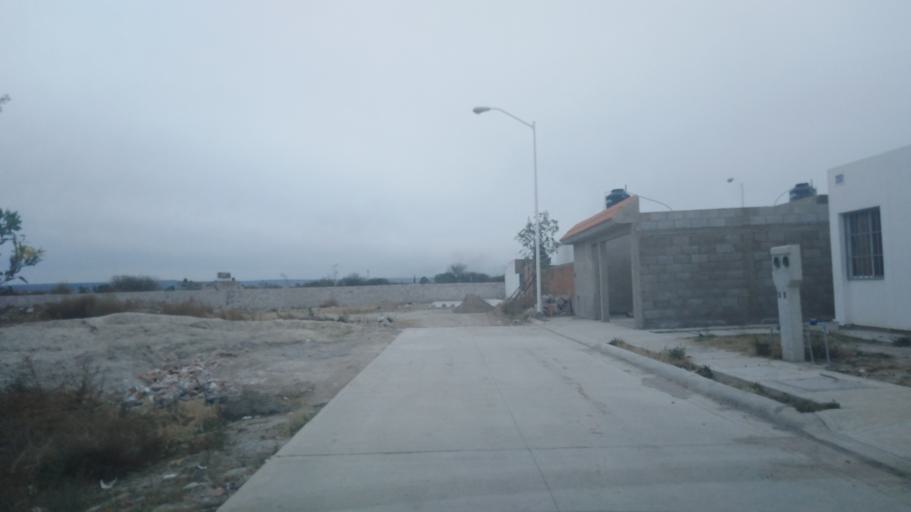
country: MX
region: Durango
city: Victoria de Durango
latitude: 24.0229
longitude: -104.6181
